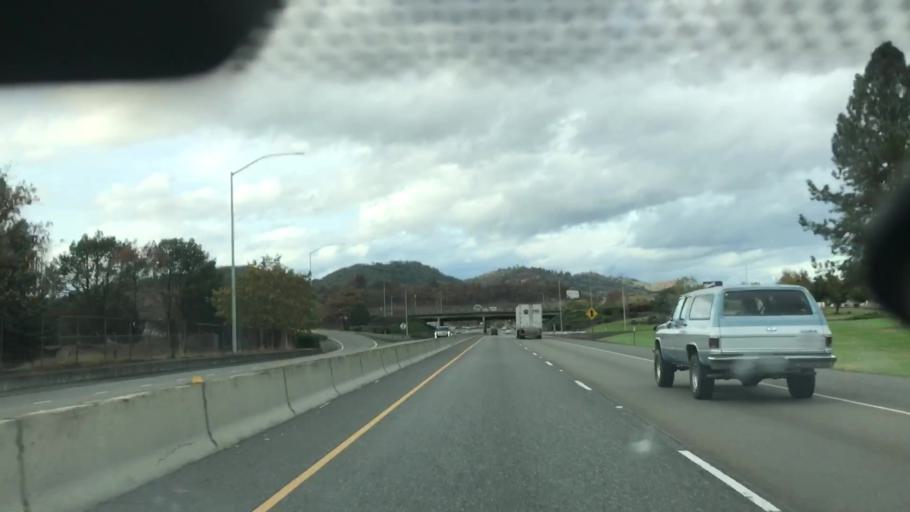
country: US
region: Oregon
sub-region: Douglas County
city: Roseburg
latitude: 43.2243
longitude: -123.3601
